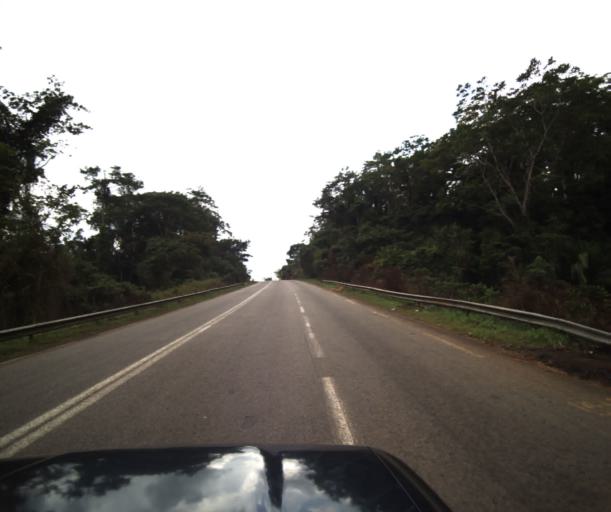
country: CM
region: Littoral
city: Edea
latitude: 3.8301
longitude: 10.3989
